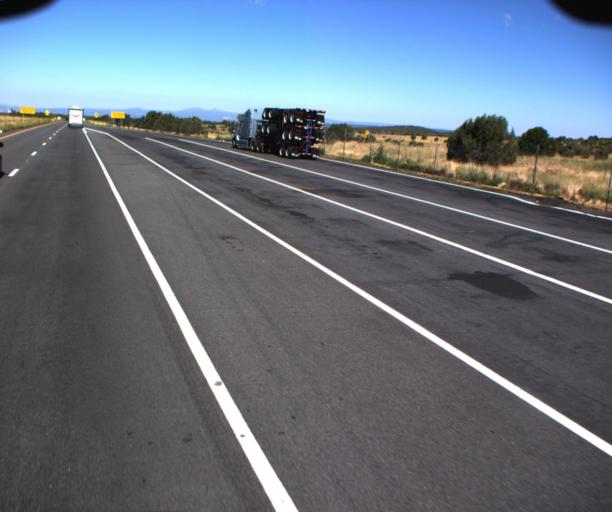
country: US
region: Arizona
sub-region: Coconino County
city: Williams
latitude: 35.2219
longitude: -112.3159
